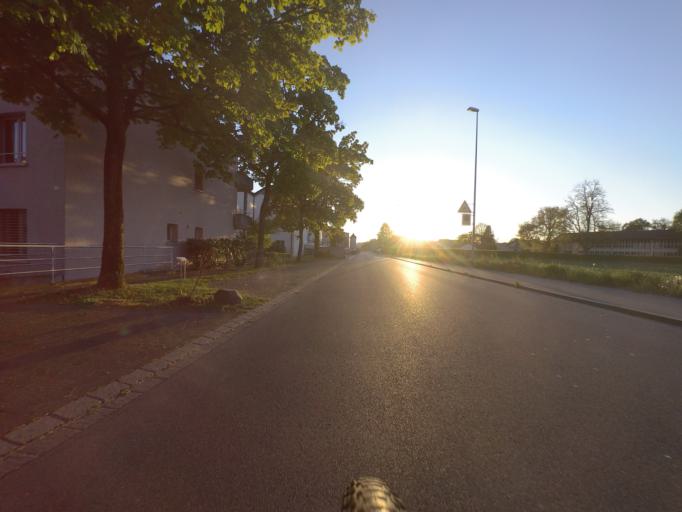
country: CH
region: Thurgau
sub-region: Frauenfeld District
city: Frauenfeld
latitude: 47.5566
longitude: 8.8859
